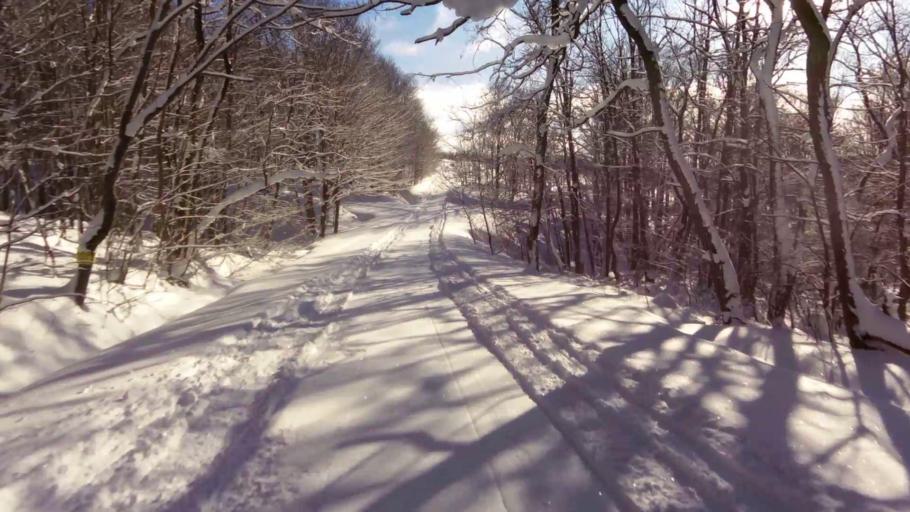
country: US
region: New York
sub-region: Chautauqua County
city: Falconer
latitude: 42.2608
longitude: -79.1800
